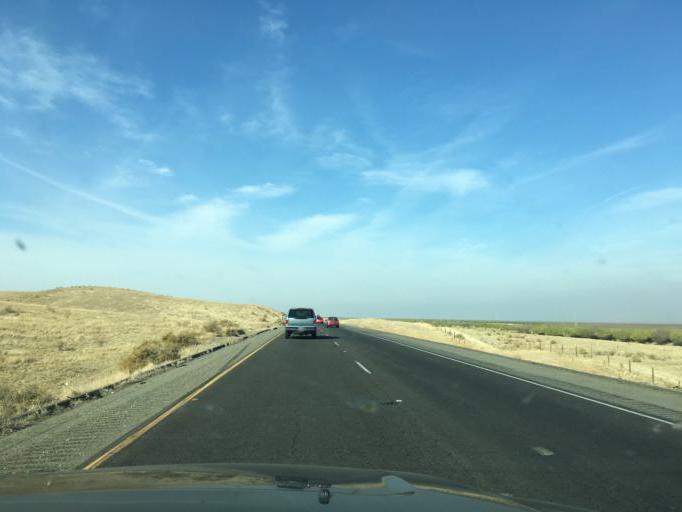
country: US
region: California
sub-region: Fresno County
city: Mendota
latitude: 36.4844
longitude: -120.4385
